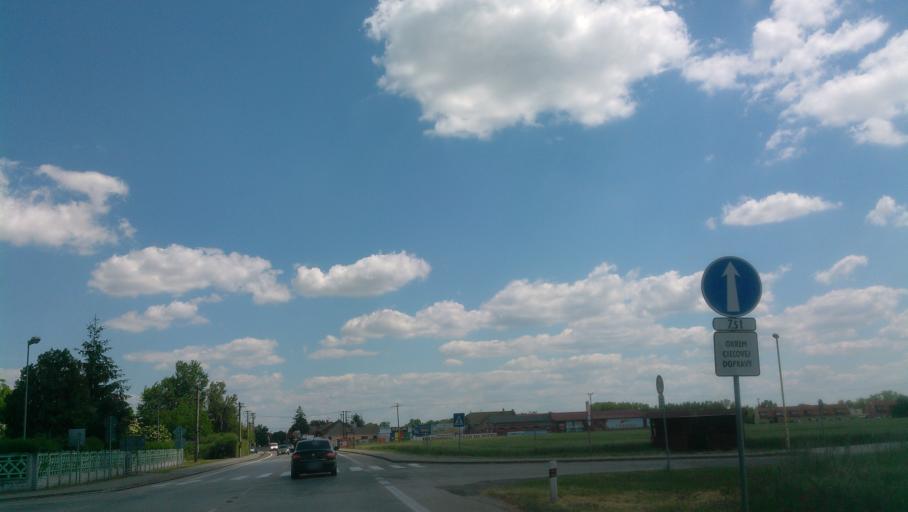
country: SK
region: Trnavsky
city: Dunajska Streda
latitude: 47.9792
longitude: 17.6541
